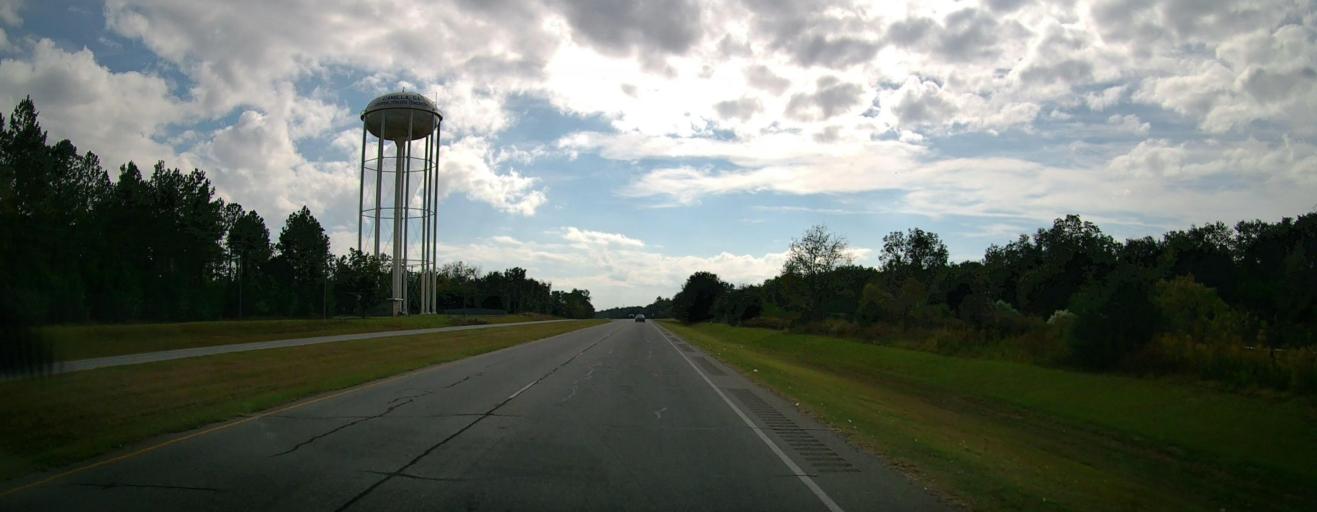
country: US
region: Georgia
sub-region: Mitchell County
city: Camilla
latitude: 31.2768
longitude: -84.1900
